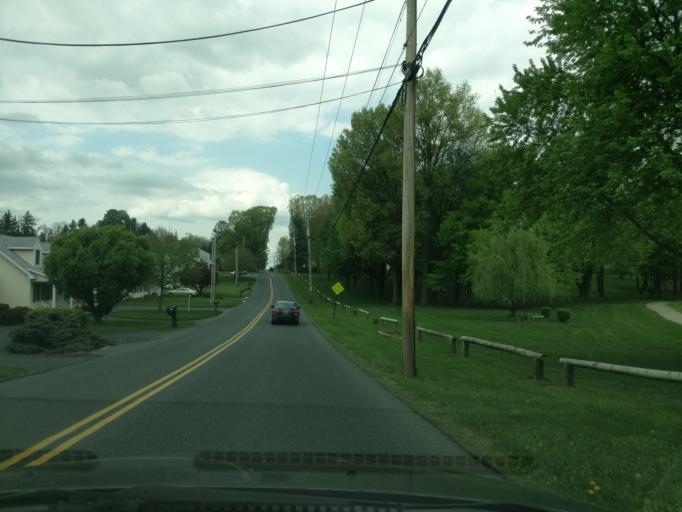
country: US
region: Pennsylvania
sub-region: Lebanon County
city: Lebanon South
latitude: 40.3234
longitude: -76.4105
